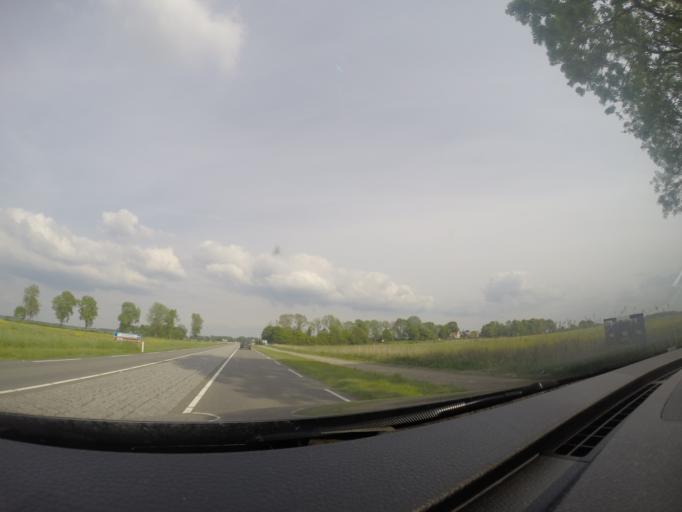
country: NL
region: Flevoland
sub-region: Gemeente Noordoostpolder
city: Ens
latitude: 52.6373
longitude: 5.7743
